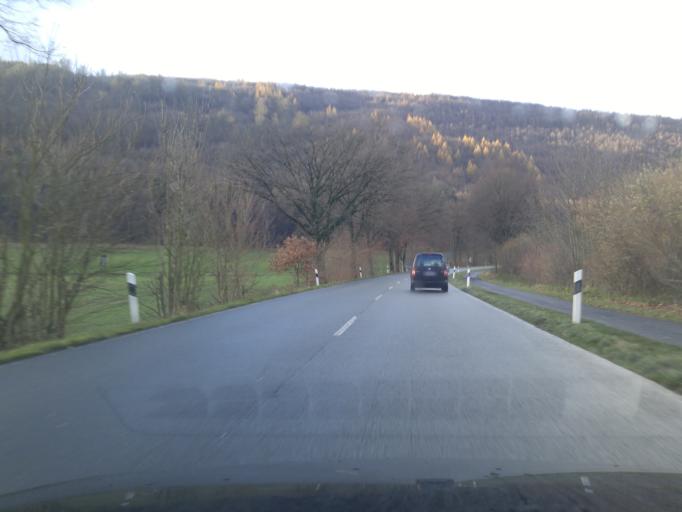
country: DE
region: Lower Saxony
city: Hannoversch Munden
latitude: 51.4505
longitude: 9.6337
